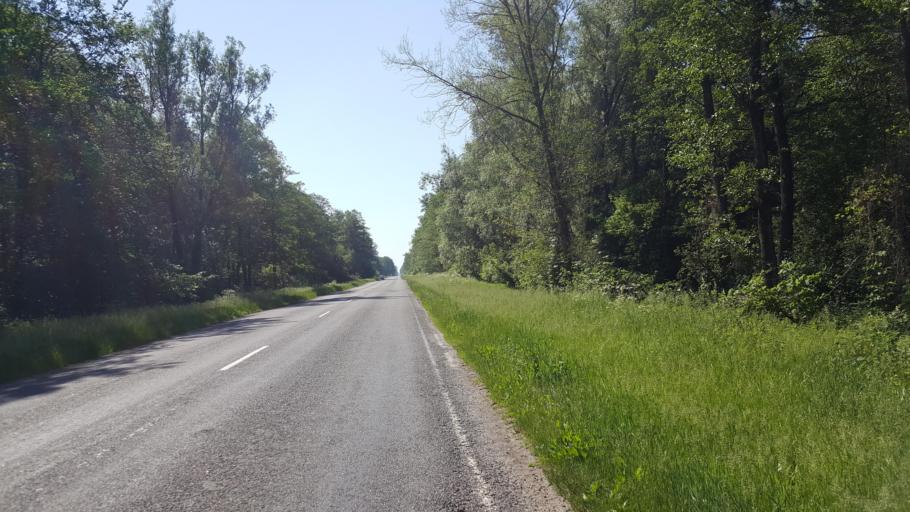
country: BY
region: Brest
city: Zhabinka
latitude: 52.2915
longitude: 23.9406
